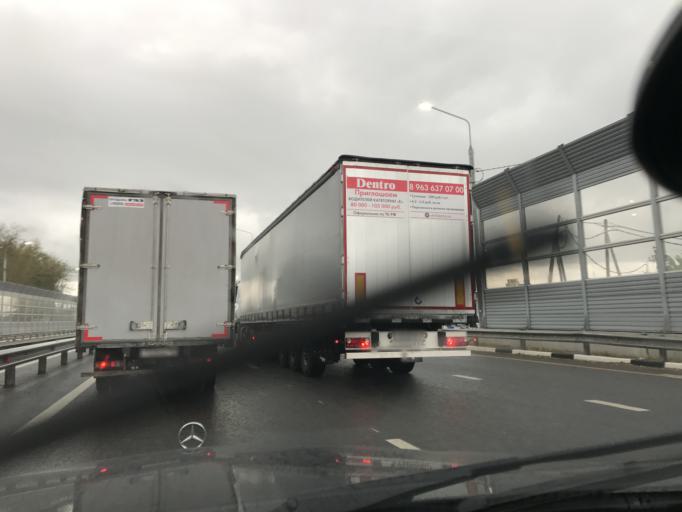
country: RU
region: Vladimir
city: Sobinka
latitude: 56.0269
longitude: 39.9992
